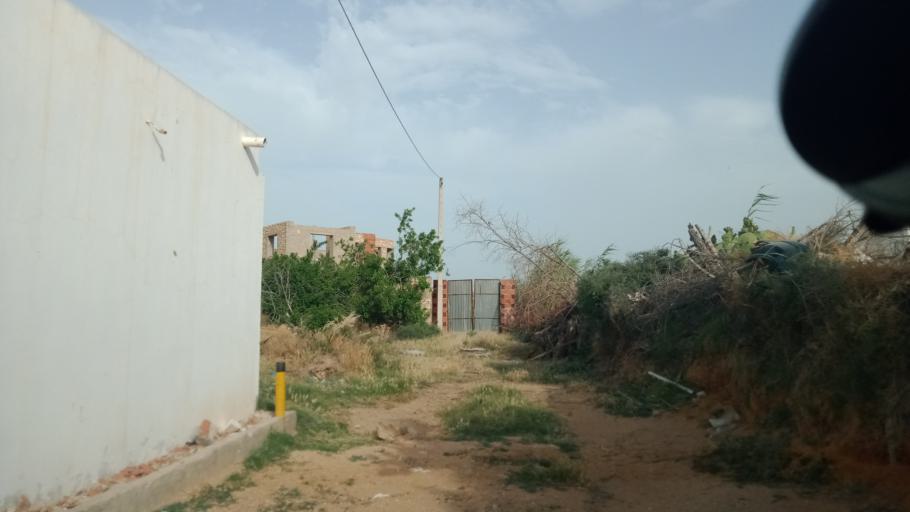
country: TN
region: Safaqis
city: Al Qarmadah
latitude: 34.7874
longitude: 10.7684
